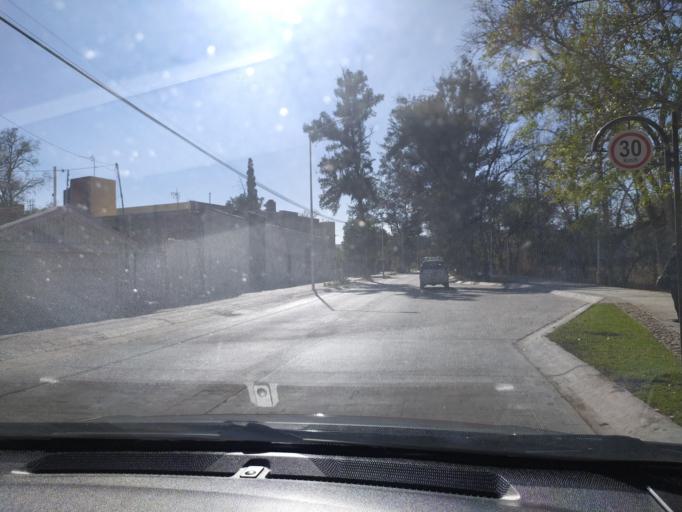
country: LA
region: Oudomxai
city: Muang La
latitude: 21.0245
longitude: 101.8413
